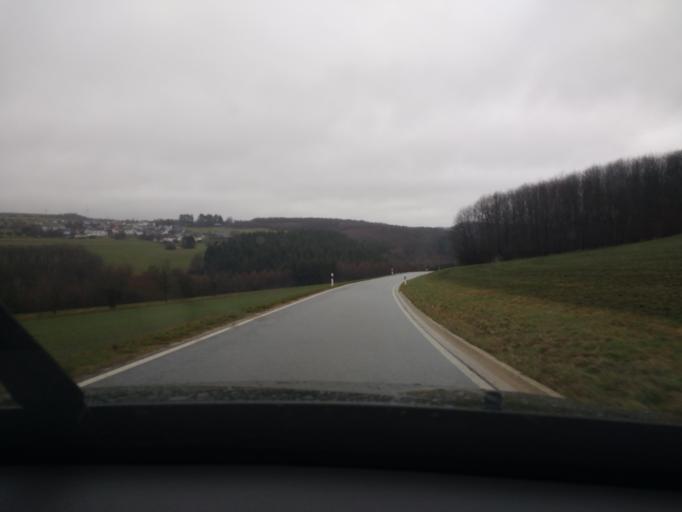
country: DE
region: Rheinland-Pfalz
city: Paschel
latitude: 49.6313
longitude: 6.6902
